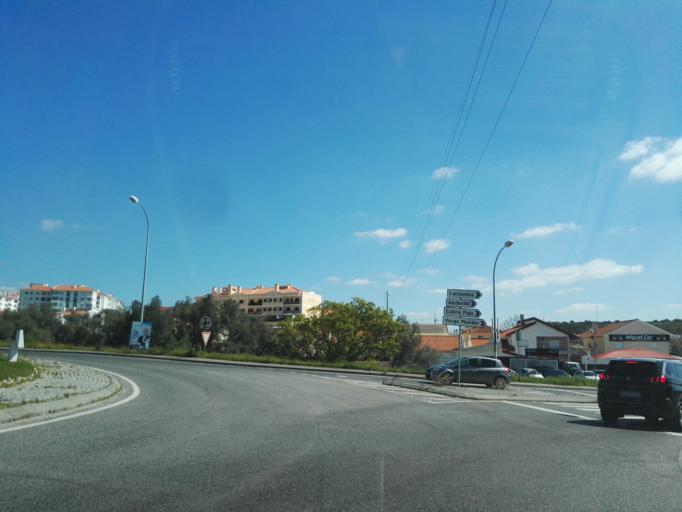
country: PT
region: Lisbon
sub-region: Sintra
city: Rio de Mouro
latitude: 38.7541
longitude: -9.3438
